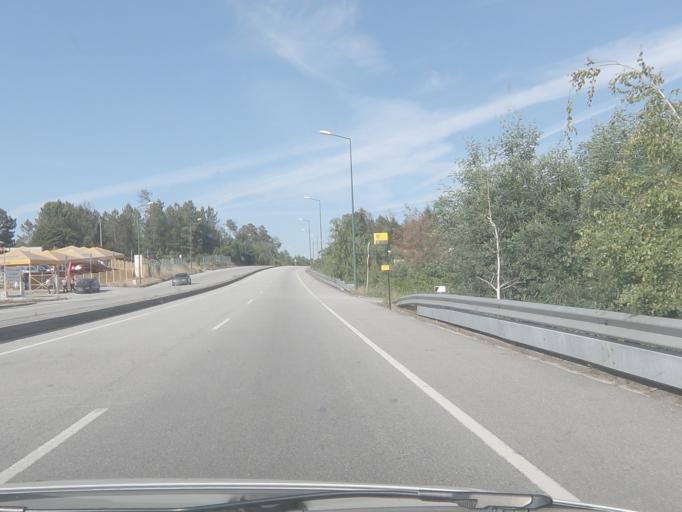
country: PT
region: Viseu
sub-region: Viseu
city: Viseu
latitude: 40.6281
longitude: -7.9403
